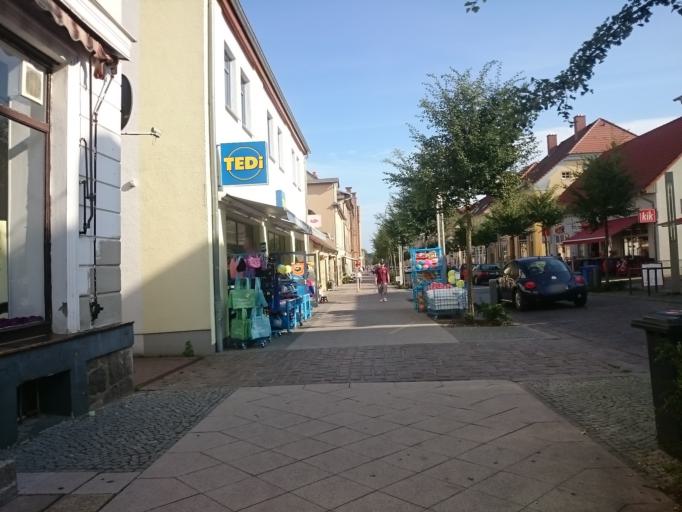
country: DE
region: Mecklenburg-Vorpommern
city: Neustrelitz
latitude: 53.3605
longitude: 13.0667
